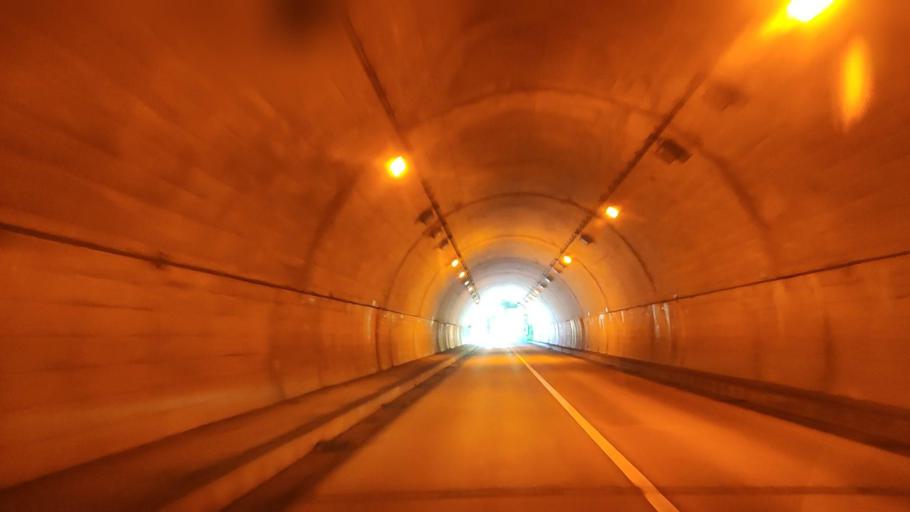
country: JP
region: Ishikawa
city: Hakui
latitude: 37.0835
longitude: 136.7308
